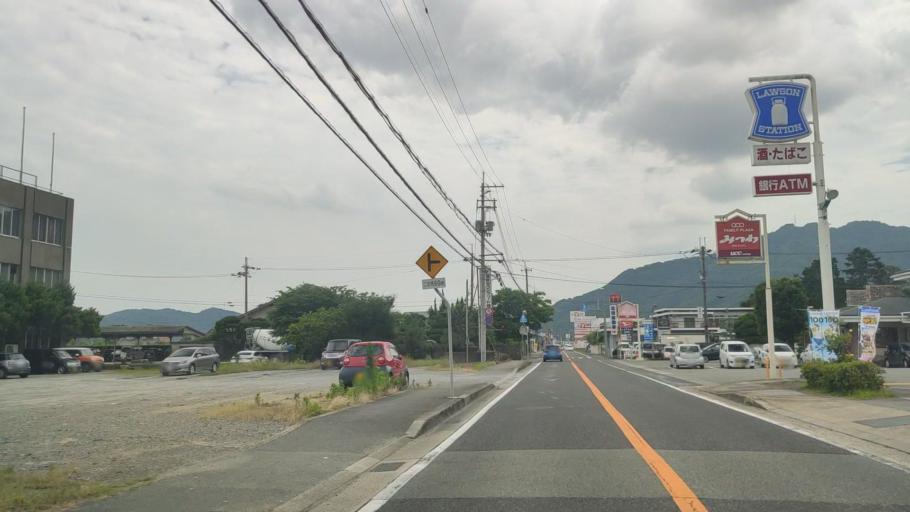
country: JP
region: Hyogo
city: Tatsunocho-tominaga
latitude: 34.9036
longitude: 134.5481
